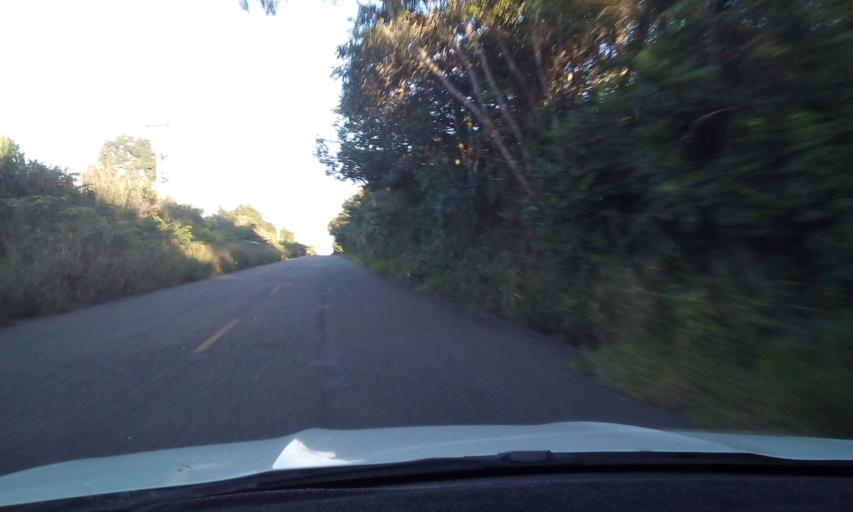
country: BR
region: Paraiba
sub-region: Areia
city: Areia
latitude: -6.9701
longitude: -35.7348
